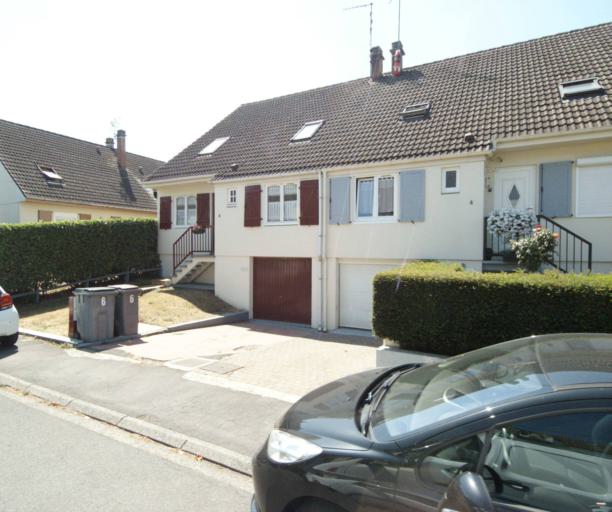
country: FR
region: Nord-Pas-de-Calais
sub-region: Departement du Nord
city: Halluin
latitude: 50.7841
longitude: 3.1142
